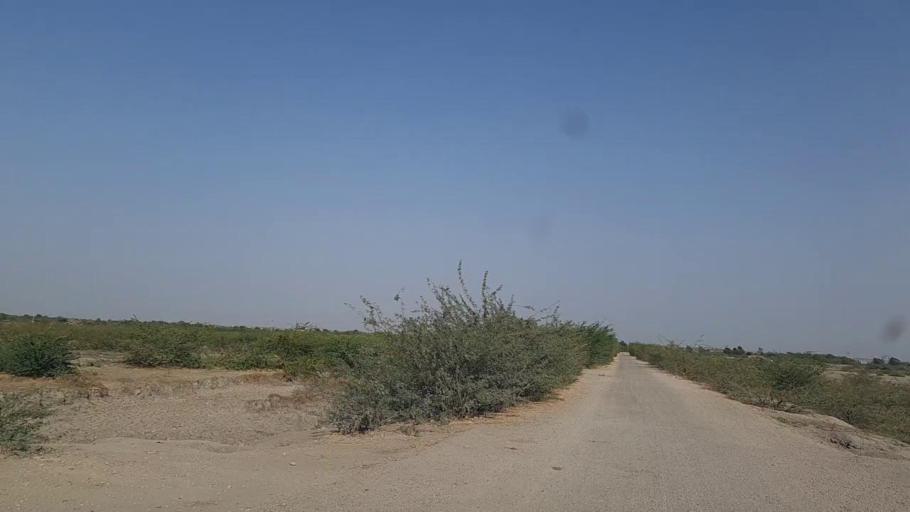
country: PK
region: Sindh
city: Naukot
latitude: 24.6040
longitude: 69.2747
